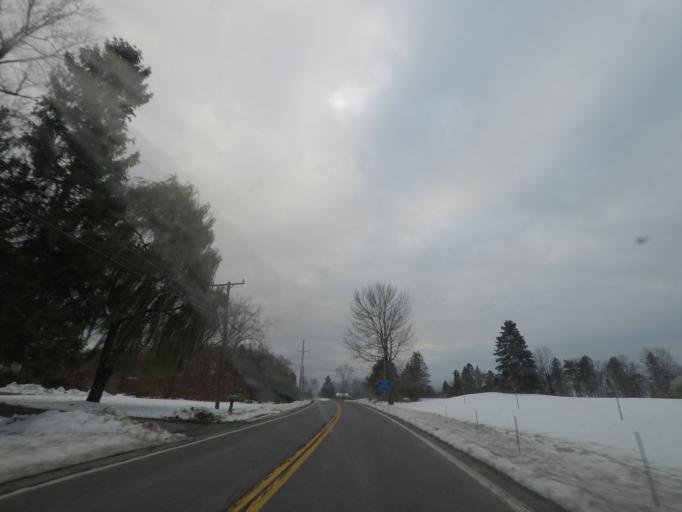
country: US
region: New York
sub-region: Ulster County
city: Clintondale
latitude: 41.6809
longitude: -74.1040
